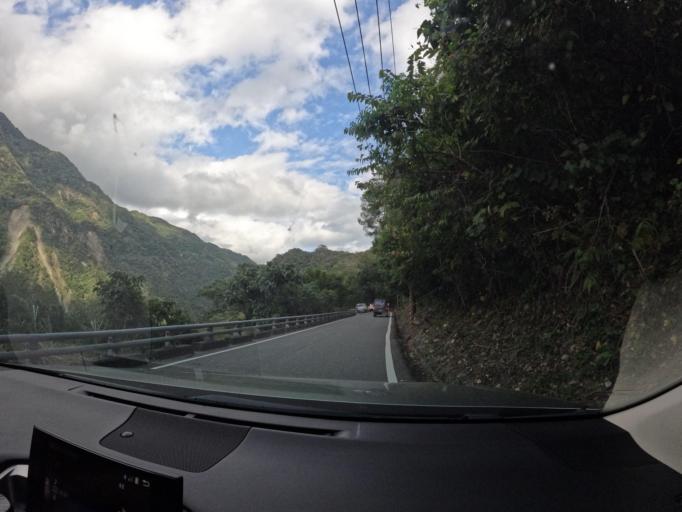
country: TW
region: Taiwan
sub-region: Taitung
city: Taitung
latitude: 23.1513
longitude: 121.0727
